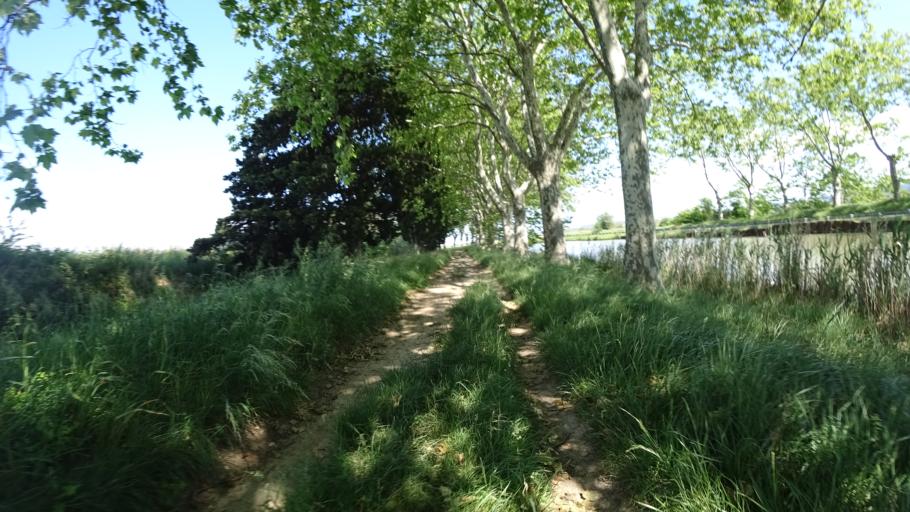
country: FR
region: Languedoc-Roussillon
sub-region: Departement de l'Aude
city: Ginestas
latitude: 43.2482
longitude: 2.8719
